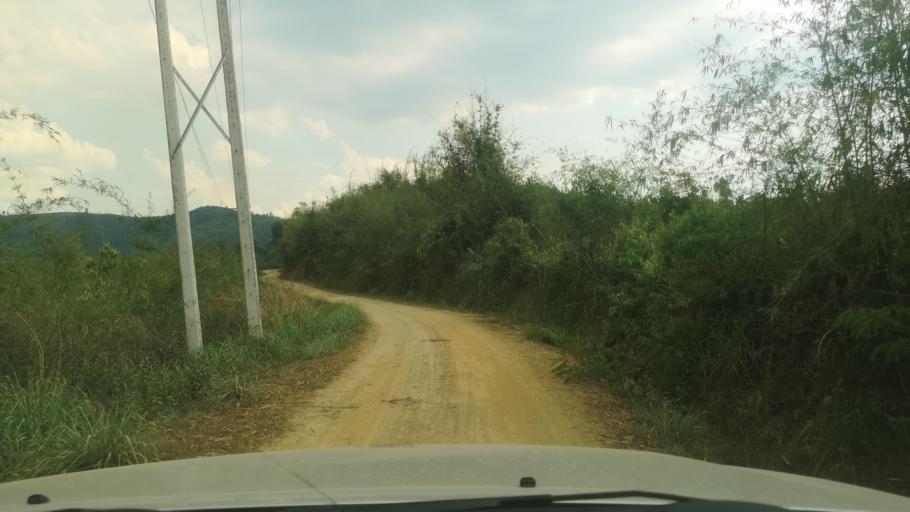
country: LA
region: Loungnamtha
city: Muang Nale
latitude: 20.3269
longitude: 101.3361
